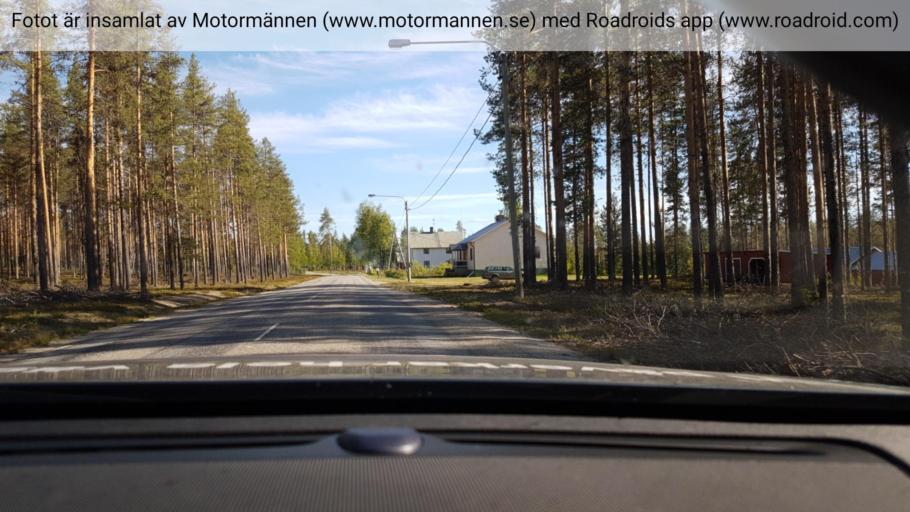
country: SE
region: Vaesterbotten
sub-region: Norsjo Kommun
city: Norsjoe
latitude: 64.6544
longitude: 19.2744
